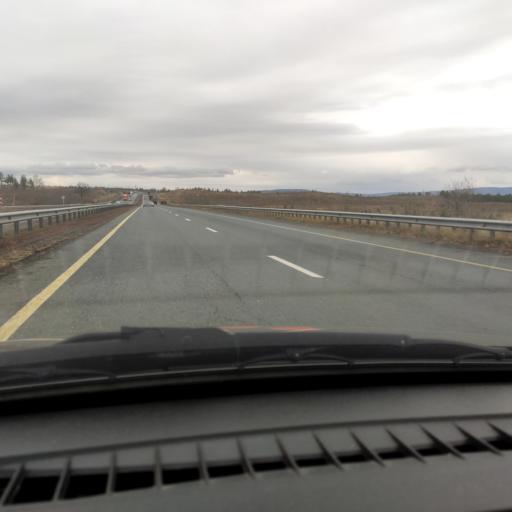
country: RU
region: Samara
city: Zhigulevsk
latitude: 53.5121
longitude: 49.5376
